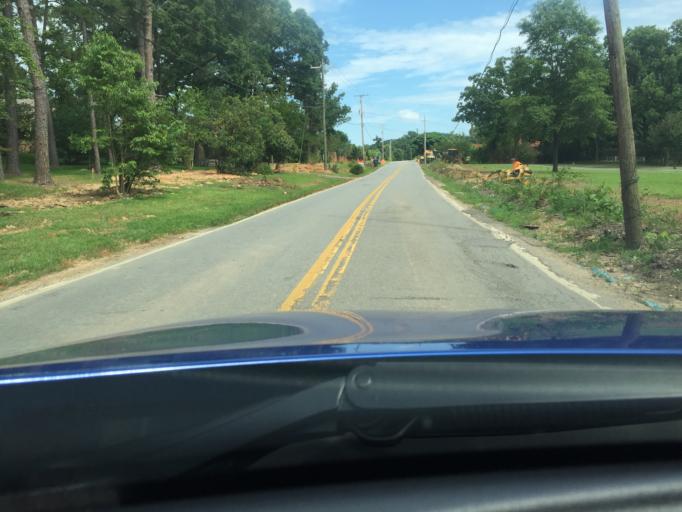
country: US
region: Arkansas
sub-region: Pulaski County
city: Maumelle
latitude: 34.8064
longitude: -92.4376
